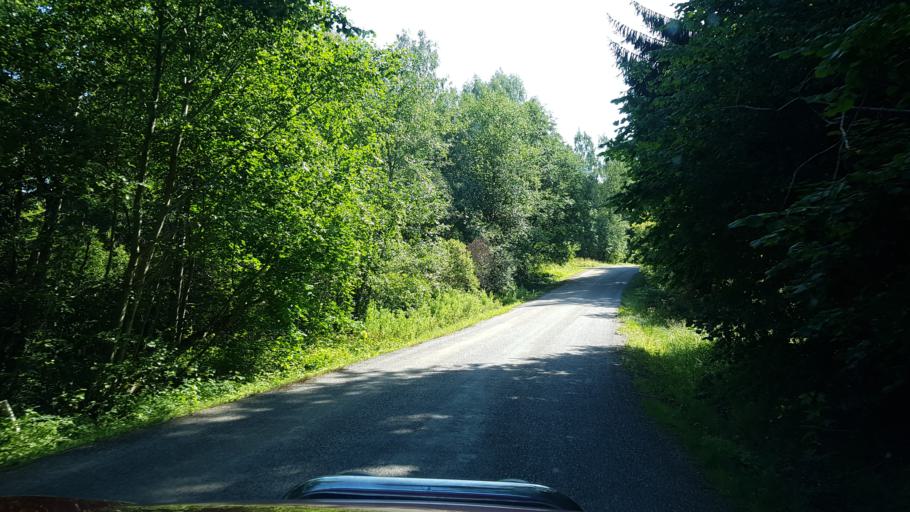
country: EE
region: Vorumaa
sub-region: Voru linn
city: Voru
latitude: 57.7098
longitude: 27.1565
